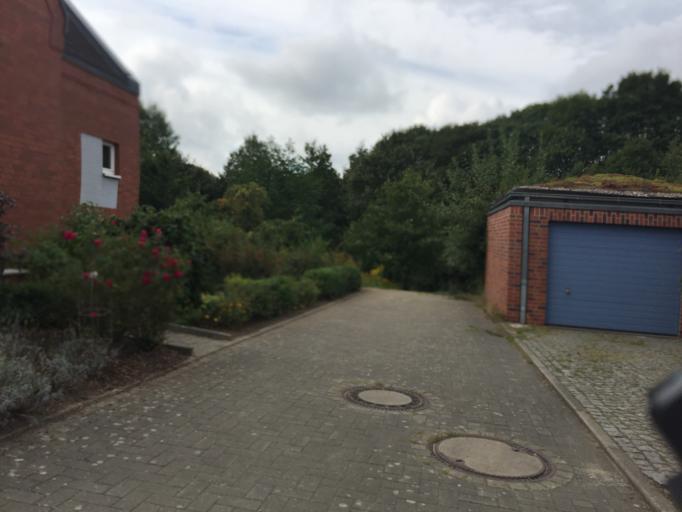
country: DE
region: Schleswig-Holstein
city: Itzehoe
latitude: 53.9340
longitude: 9.5313
